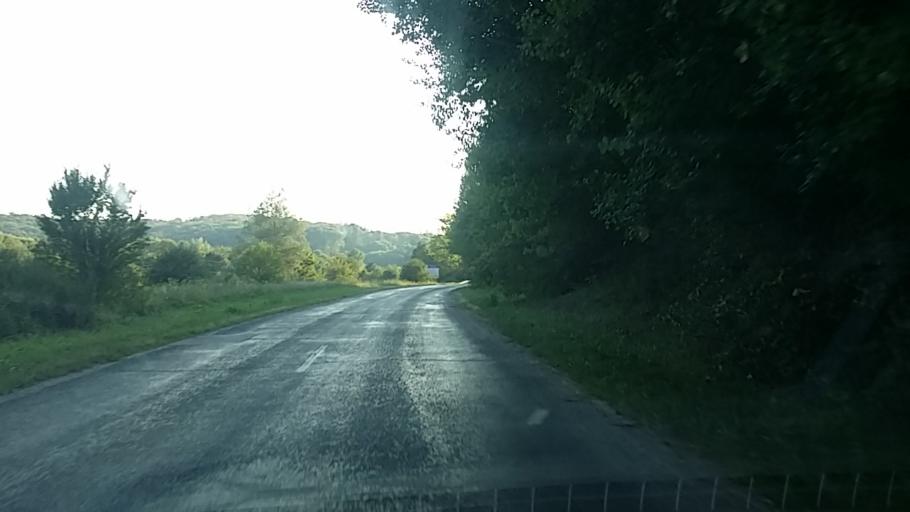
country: HU
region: Baranya
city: Sasd
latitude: 46.1548
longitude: 18.0817
